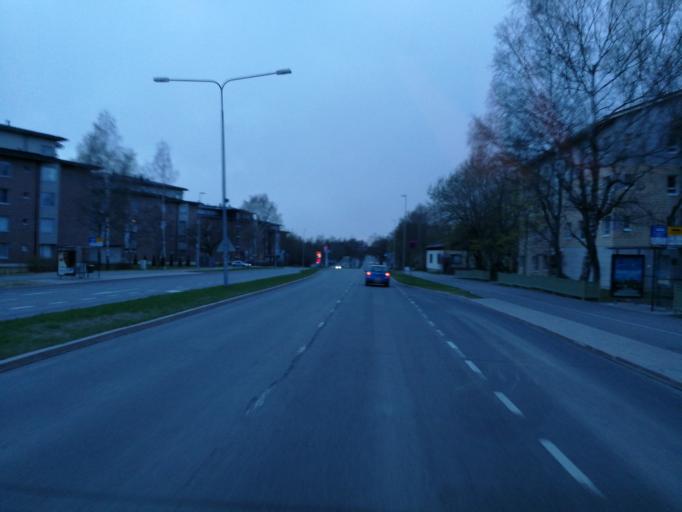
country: FI
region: Varsinais-Suomi
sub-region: Turku
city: Turku
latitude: 60.4629
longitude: 22.2626
